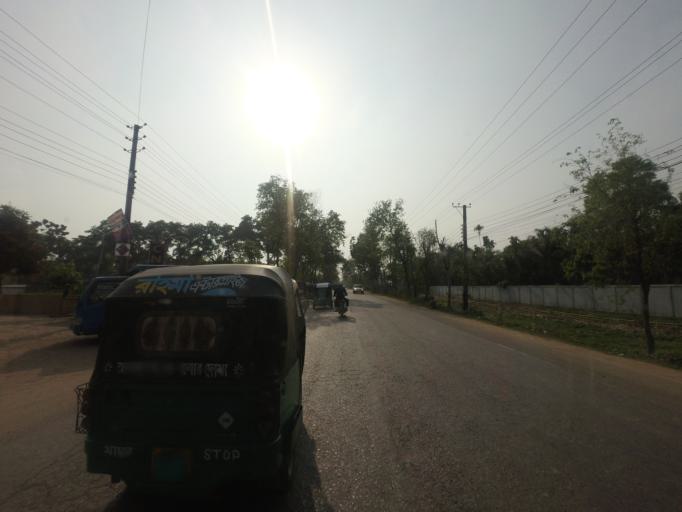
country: BD
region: Sylhet
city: Sylhet
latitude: 24.9154
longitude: 91.9461
